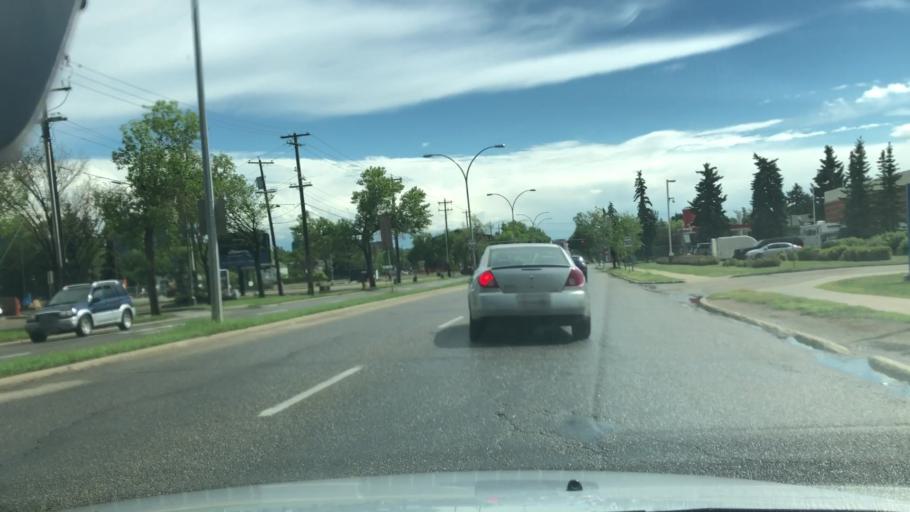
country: CA
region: Alberta
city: Edmonton
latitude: 53.5606
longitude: -113.5084
